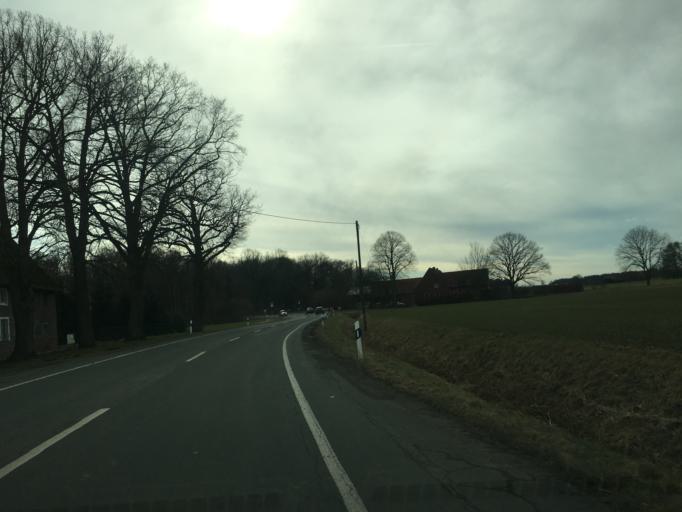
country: DE
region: North Rhine-Westphalia
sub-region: Regierungsbezirk Munster
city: Senden
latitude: 51.8471
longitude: 7.5442
